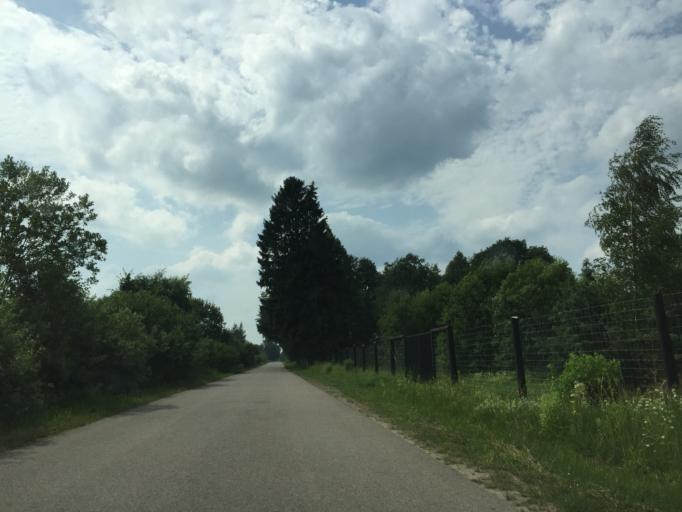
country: LV
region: Ozolnieku
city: Ozolnieki
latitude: 56.7520
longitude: 23.7228
